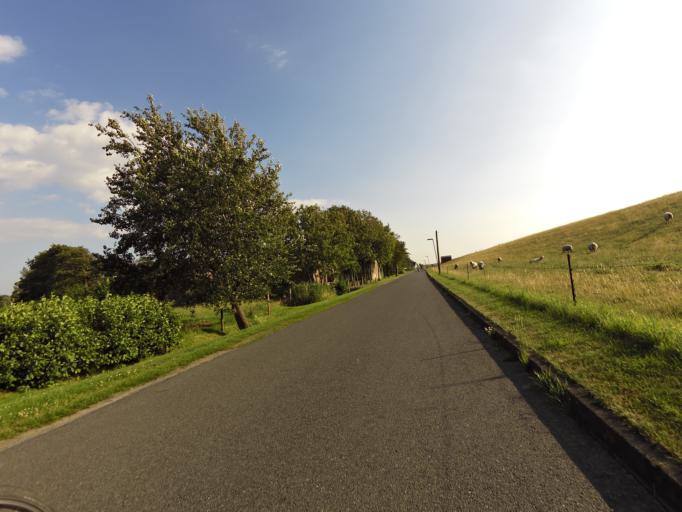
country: DE
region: Lower Saxony
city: Nordholz
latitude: 53.7894
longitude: 8.5554
